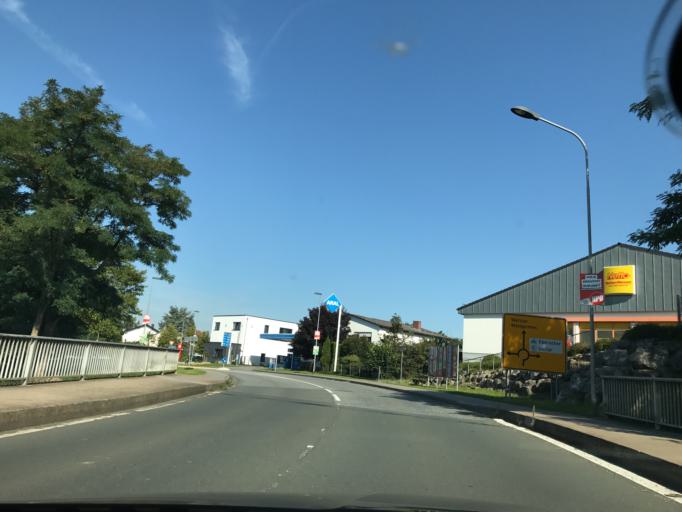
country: DE
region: Hesse
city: Allendorf an der Lahn
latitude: 50.5772
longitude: 8.5650
